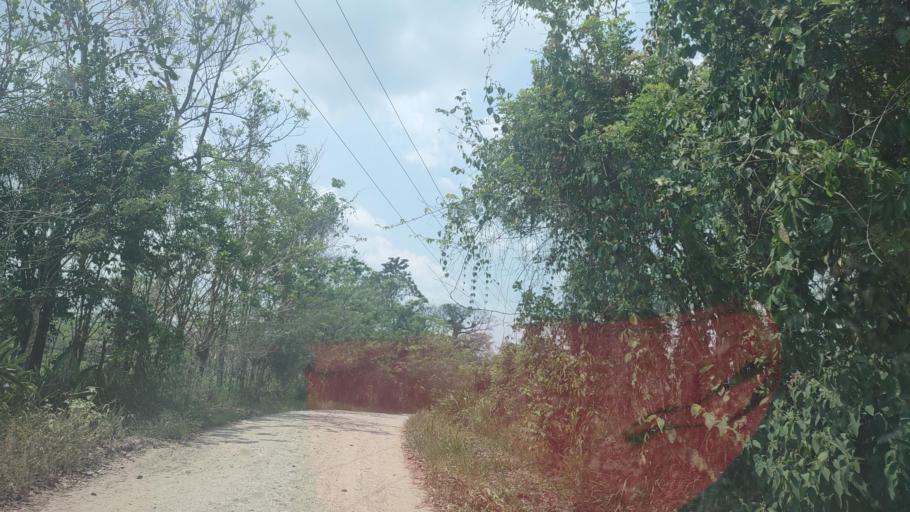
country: MX
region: Chiapas
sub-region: Tecpatan
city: Raudales Malpaso
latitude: 17.2711
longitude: -93.8718
